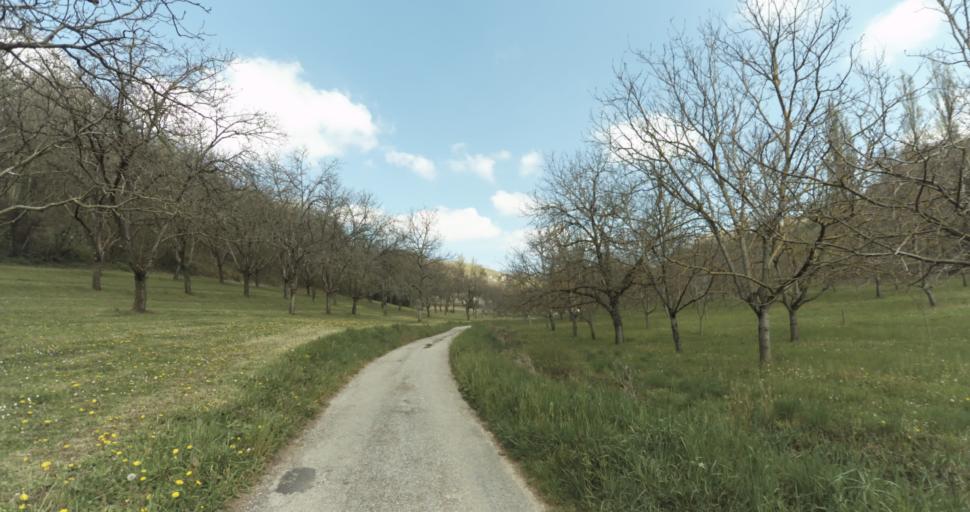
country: FR
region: Rhone-Alpes
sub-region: Departement de l'Isere
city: Saint-Verand
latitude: 45.1717
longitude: 5.3145
